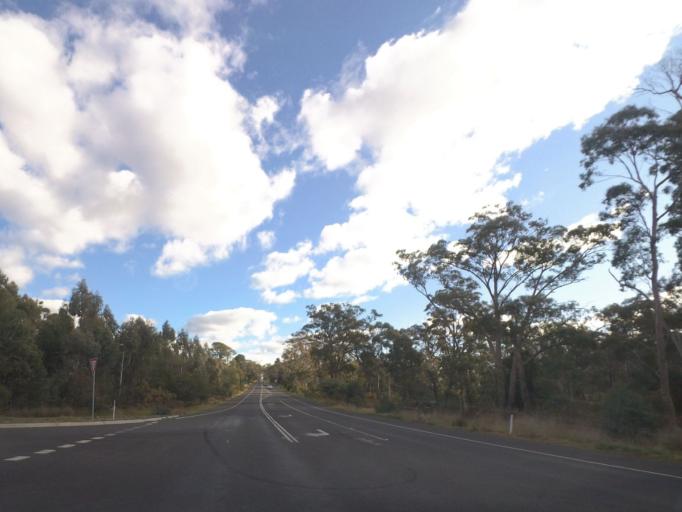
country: AU
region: Victoria
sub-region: Mount Alexander
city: Castlemaine
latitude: -37.1032
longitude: 144.3167
